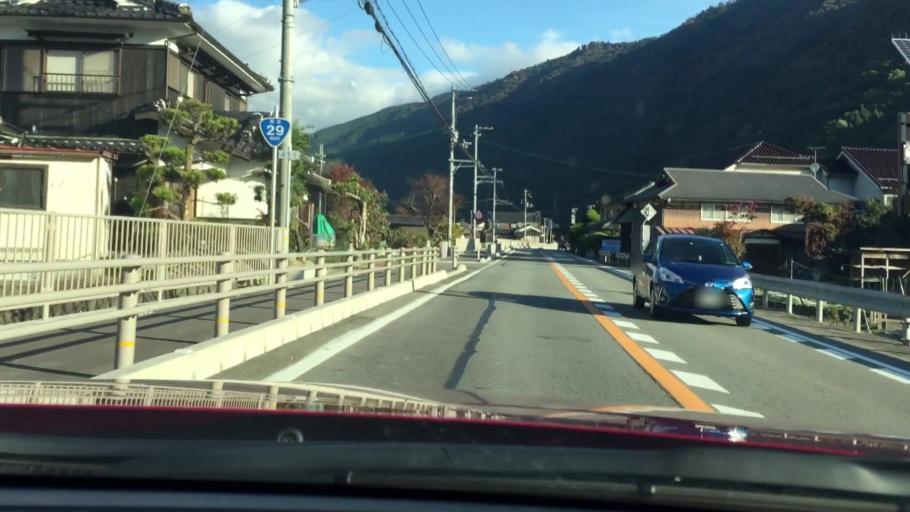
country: JP
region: Hyogo
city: Yamazakicho-nakabirose
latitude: 35.1183
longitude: 134.5684
